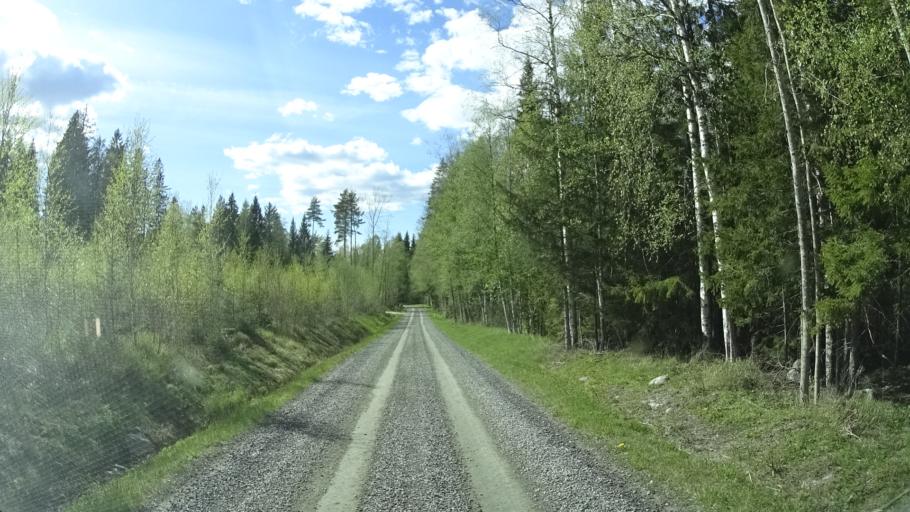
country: SE
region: OErebro
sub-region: Nora Kommun
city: As
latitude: 59.4421
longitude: 14.8385
